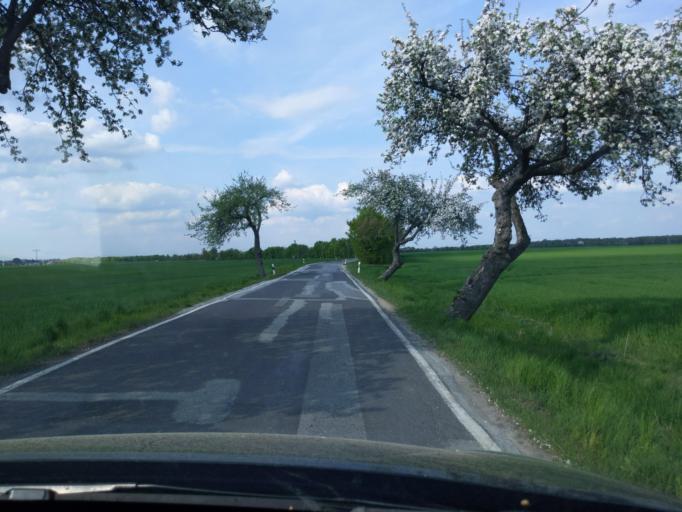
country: DE
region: Saxony
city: Malschwitz
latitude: 51.2206
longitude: 14.5295
